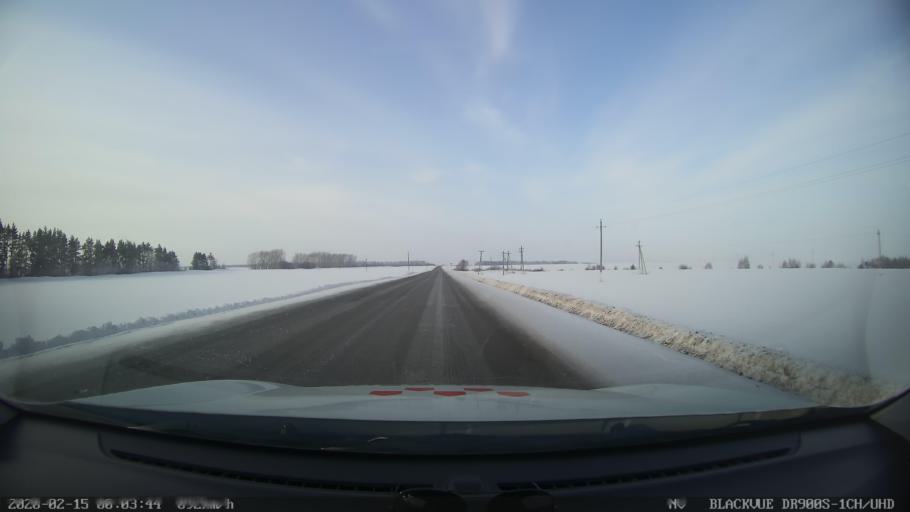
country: RU
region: Tatarstan
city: Kuybyshevskiy Zaton
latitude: 55.3750
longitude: 48.9937
